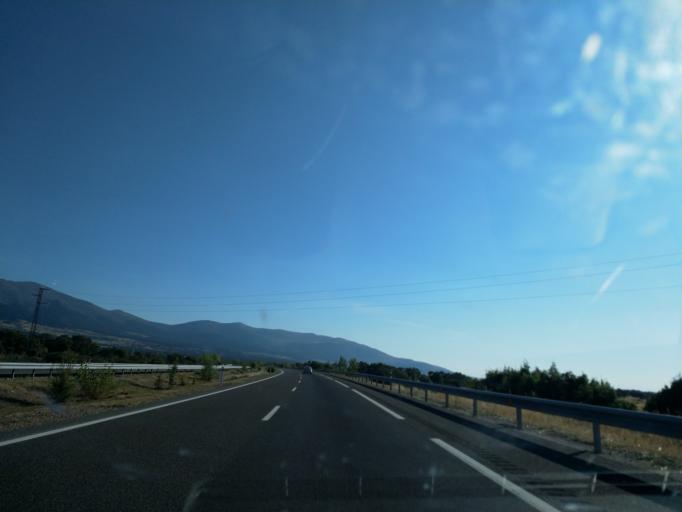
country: ES
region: Castille and Leon
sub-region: Provincia de Segovia
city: Segovia
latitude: 40.8898
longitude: -4.1156
